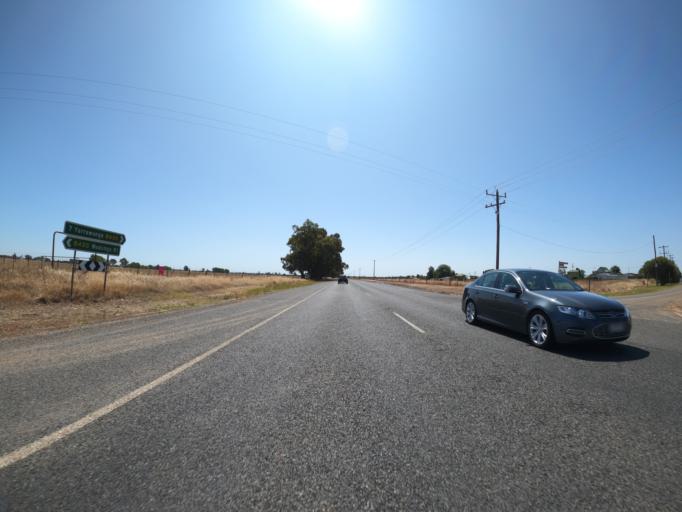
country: AU
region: Victoria
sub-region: Moira
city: Yarrawonga
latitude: -36.0253
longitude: 146.0670
